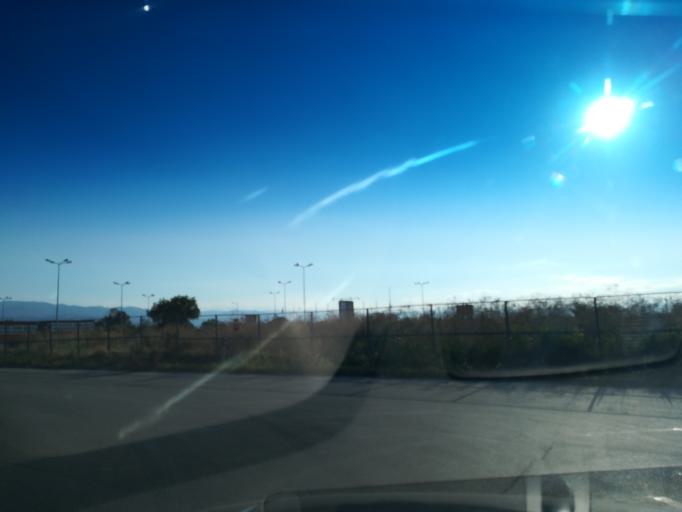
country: BG
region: Plovdiv
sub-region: Obshtina Plovdiv
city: Plovdiv
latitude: 42.1598
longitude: 24.6790
